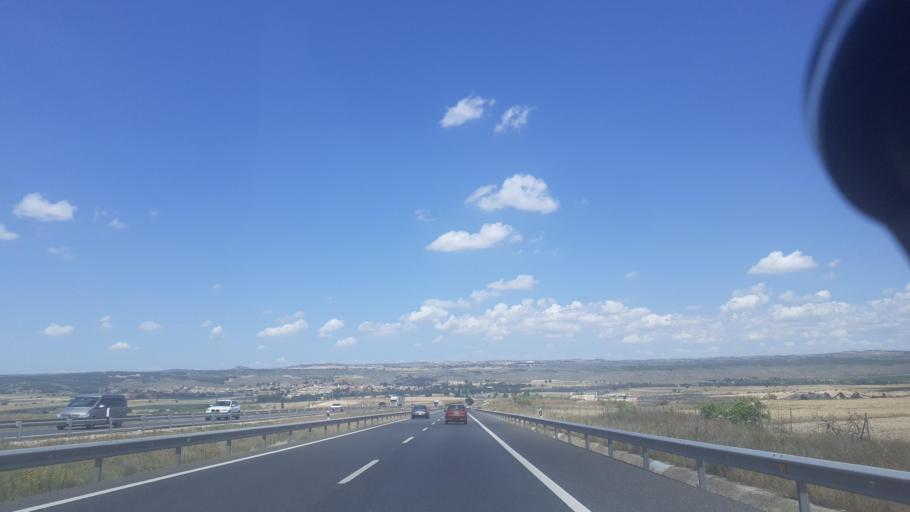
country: ES
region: Madrid
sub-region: Provincia de Madrid
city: Fuentiduena de Tajo
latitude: 40.1003
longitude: -3.1339
